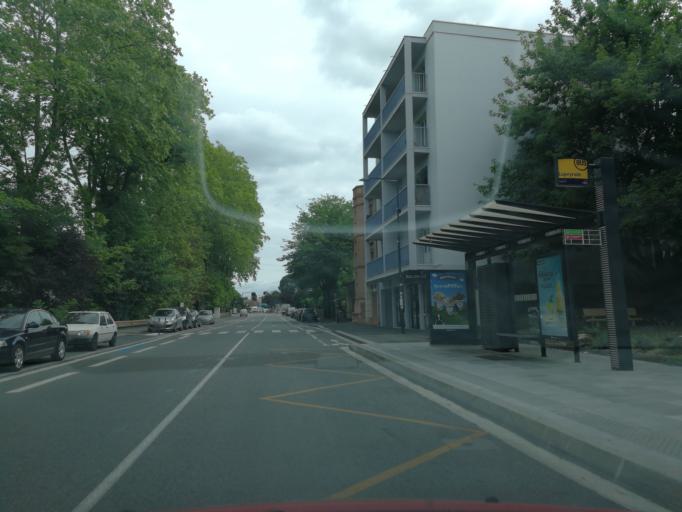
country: FR
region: Midi-Pyrenees
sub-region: Departement de la Haute-Garonne
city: Ramonville-Saint-Agne
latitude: 43.5498
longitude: 1.4709
